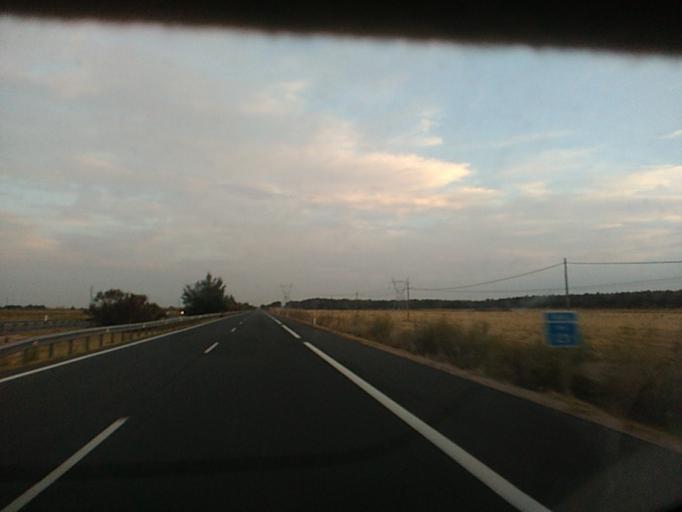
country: ES
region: Castille and Leon
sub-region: Provincia de Avila
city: Palacios de Goda
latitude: 41.0968
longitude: -4.7487
